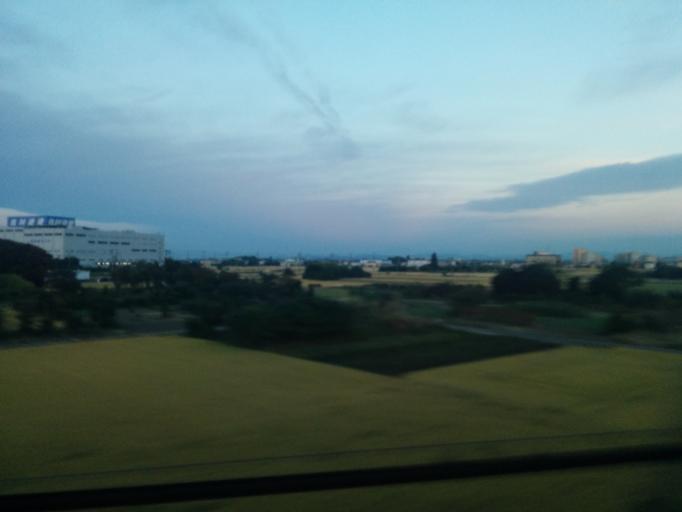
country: JP
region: Aichi
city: Inazawa
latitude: 35.2628
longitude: 136.7598
